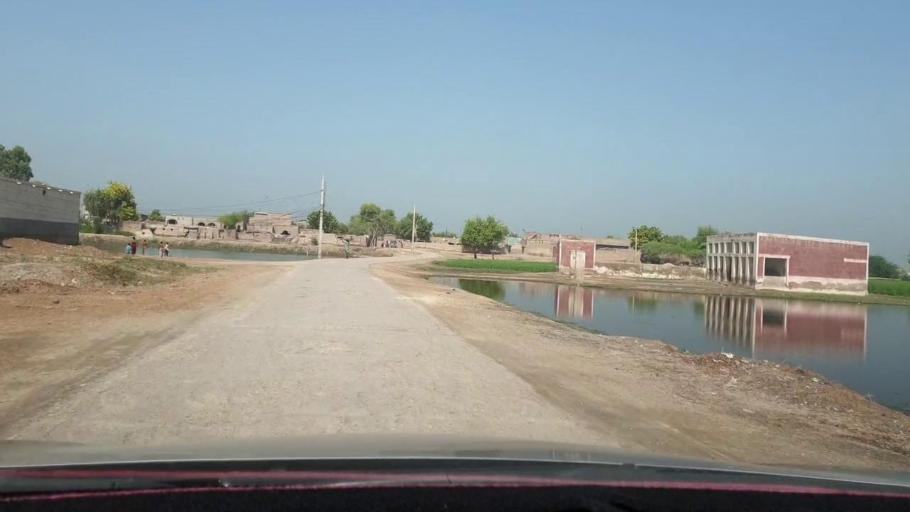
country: PK
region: Sindh
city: Kambar
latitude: 27.5994
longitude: 67.9769
